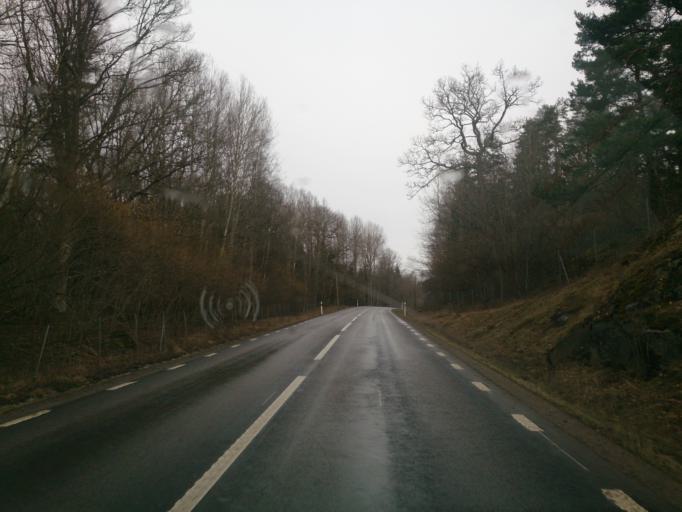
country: SE
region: OEstergoetland
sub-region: Atvidabergs Kommun
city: Atvidaberg
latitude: 58.1799
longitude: 16.0254
